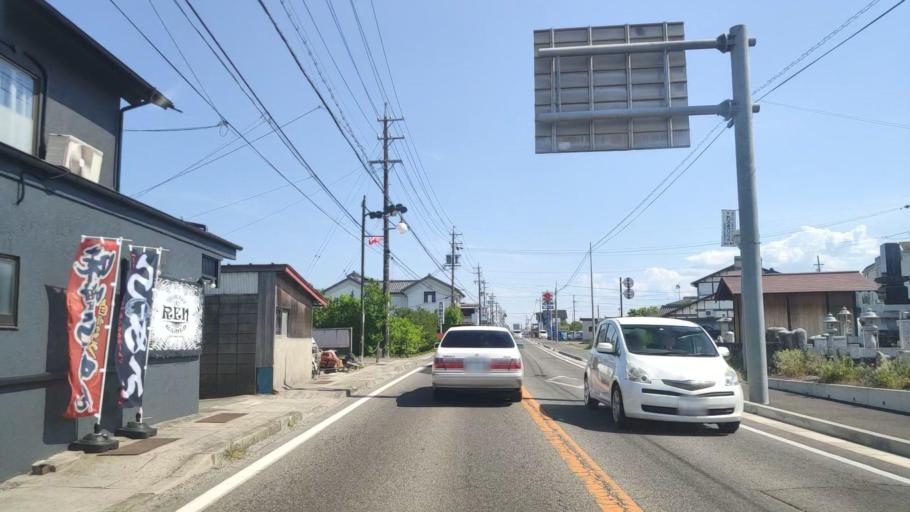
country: JP
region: Nagano
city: Hotaka
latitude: 36.3444
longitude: 137.8864
